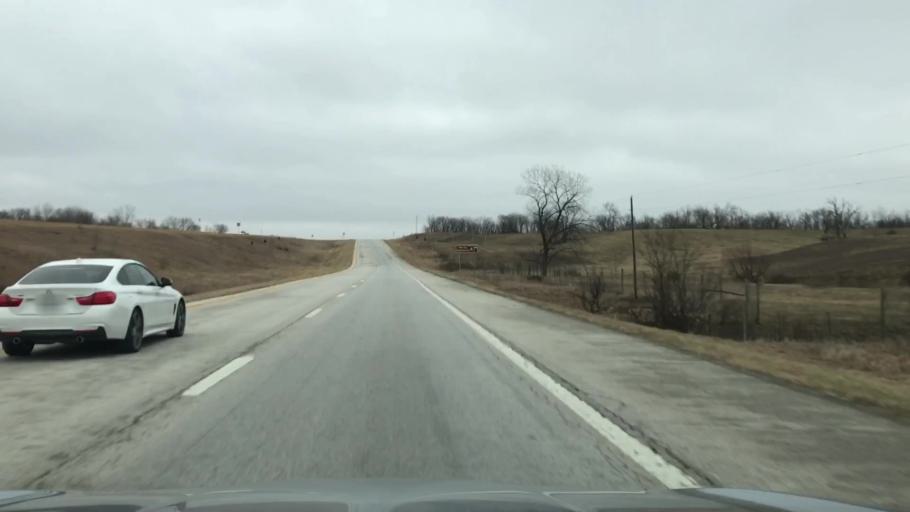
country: US
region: Missouri
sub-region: Linn County
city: Marceline
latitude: 39.7590
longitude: -92.8756
